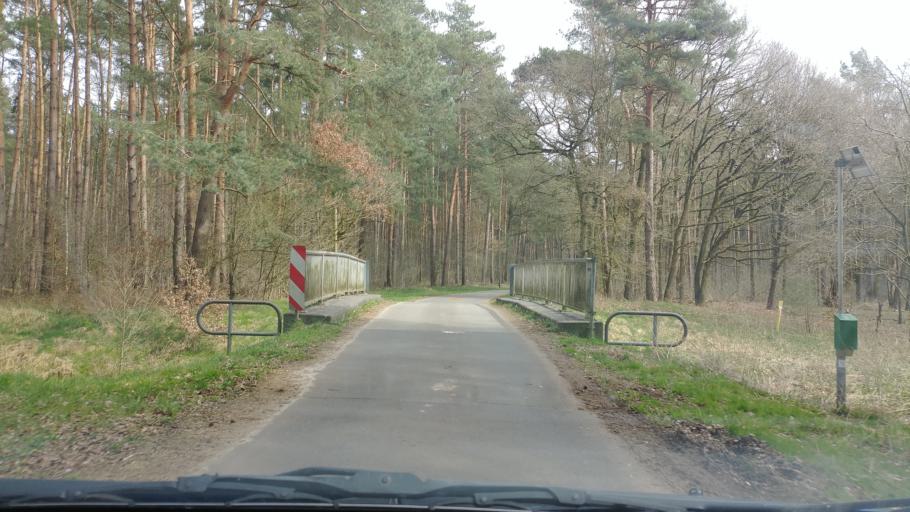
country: DE
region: Lower Saxony
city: Elze
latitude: 52.5638
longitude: 9.7997
